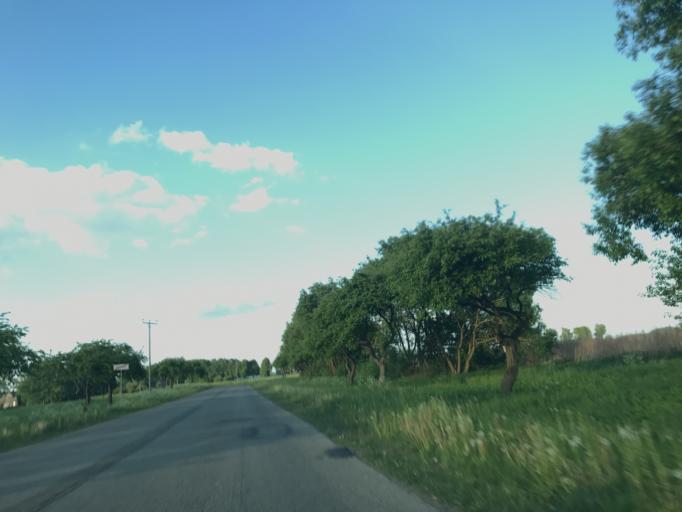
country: LV
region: Lecava
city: Iecava
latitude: 56.6023
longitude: 24.2266
